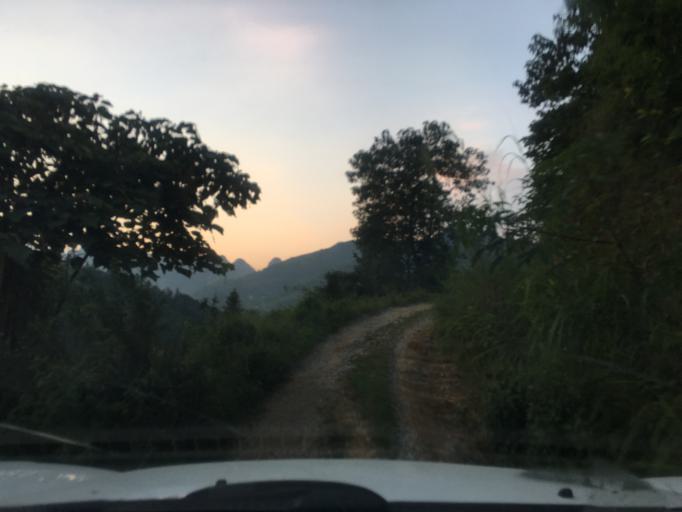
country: CN
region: Guangxi Zhuangzu Zizhiqu
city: Xinzhou
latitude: 25.3501
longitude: 105.7384
